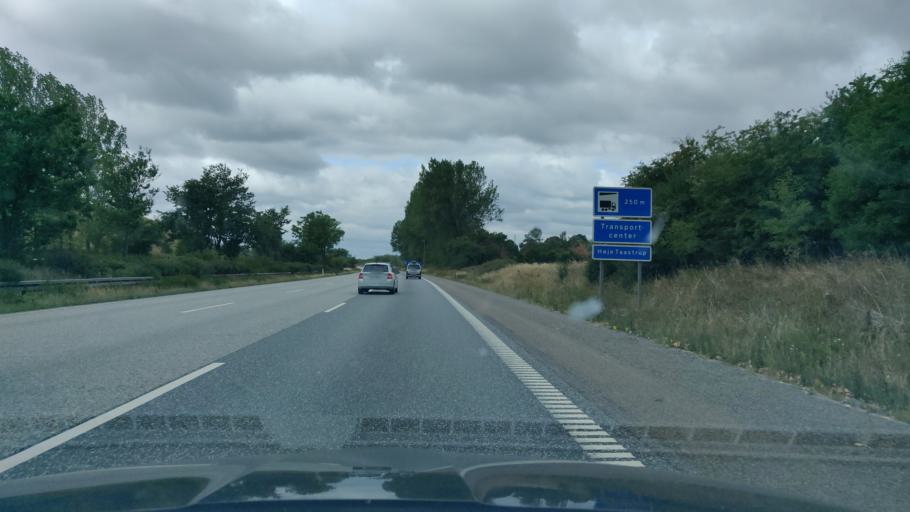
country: DK
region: Capital Region
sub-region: Hoje-Taastrup Kommune
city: Taastrup
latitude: 55.6650
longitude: 12.2480
